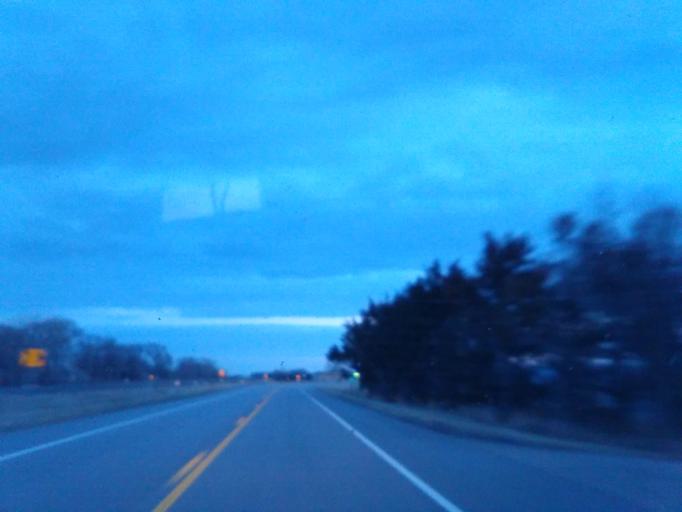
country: US
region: Nebraska
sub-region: Garden County
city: Oshkosh
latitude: 41.3284
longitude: -102.1335
